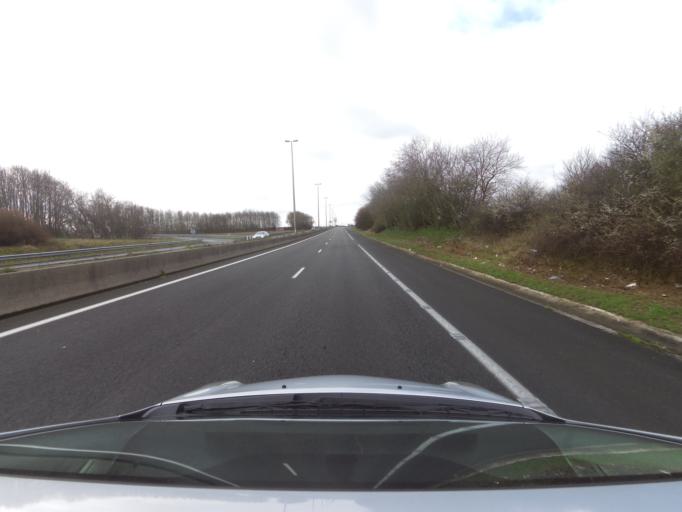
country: FR
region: Nord-Pas-de-Calais
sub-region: Departement du Pas-de-Calais
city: Coquelles
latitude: 50.9146
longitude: 1.7867
